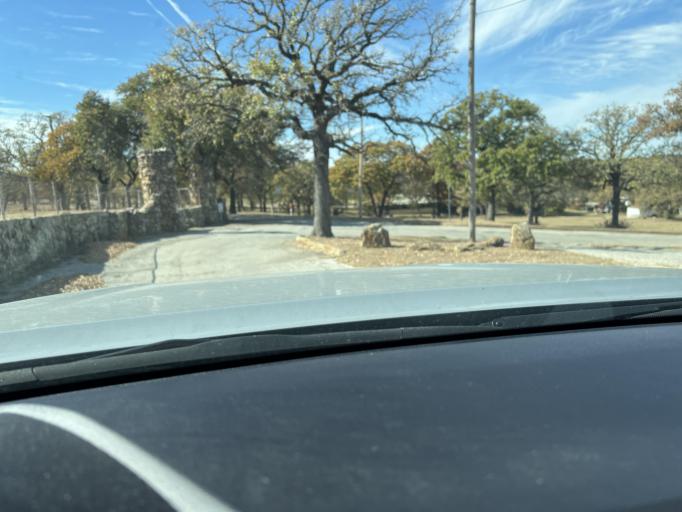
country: US
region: Texas
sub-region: Eastland County
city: Eastland
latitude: 32.3988
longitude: -98.8329
